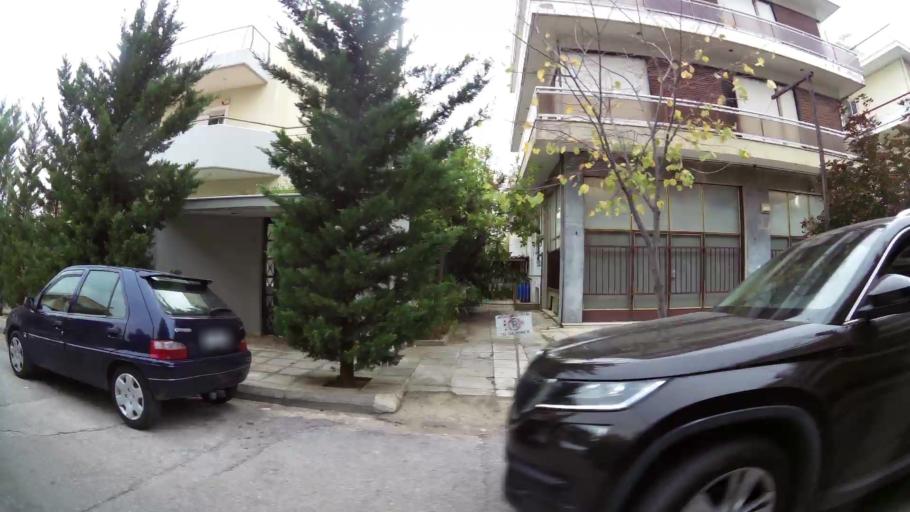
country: GR
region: Attica
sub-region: Nomarchia Athinas
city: Irakleio
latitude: 38.0417
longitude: 23.7673
